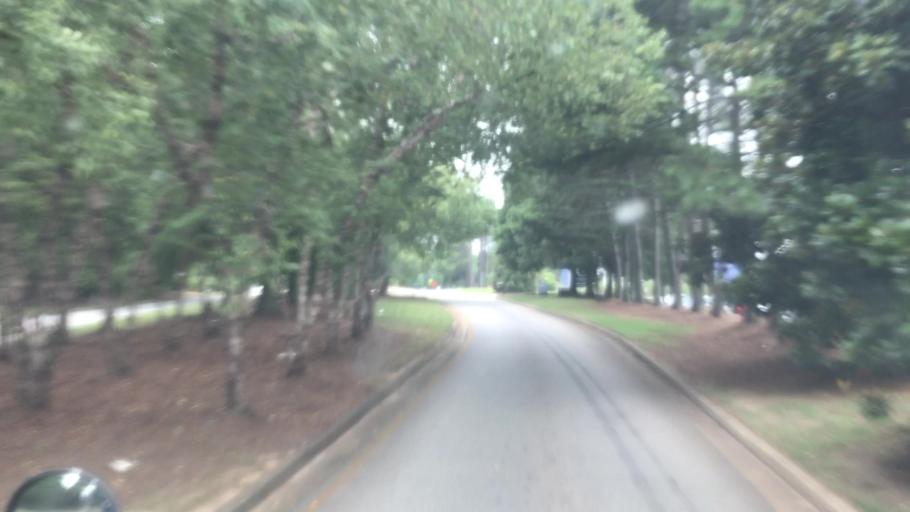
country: US
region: Georgia
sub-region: Henry County
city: McDonough
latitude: 33.3901
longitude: -84.1703
